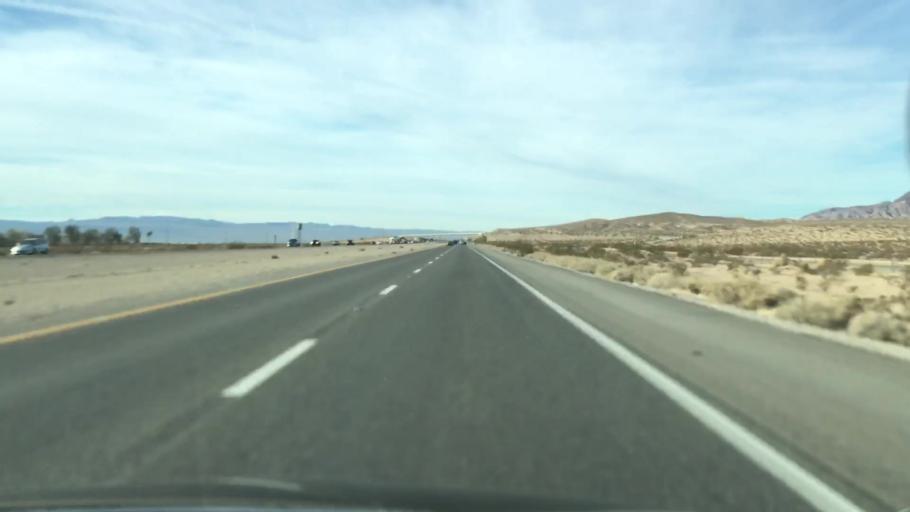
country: US
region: California
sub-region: San Bernardino County
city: Barstow
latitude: 34.9356
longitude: -116.7077
